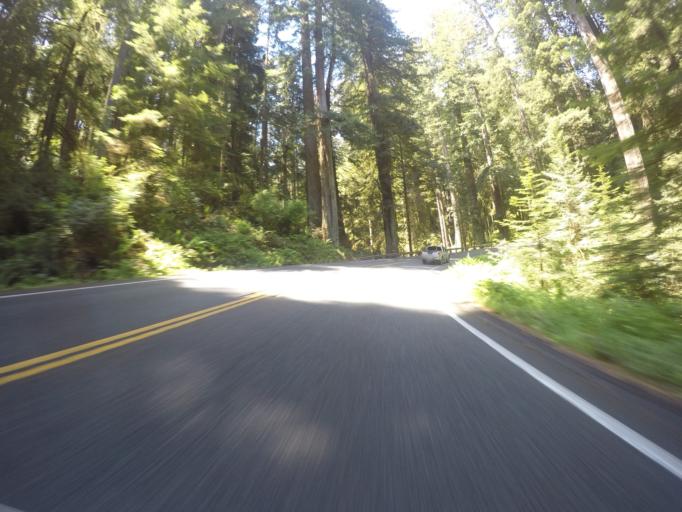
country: US
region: California
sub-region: Del Norte County
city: Bertsch-Oceanview
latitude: 41.8095
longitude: -124.1207
